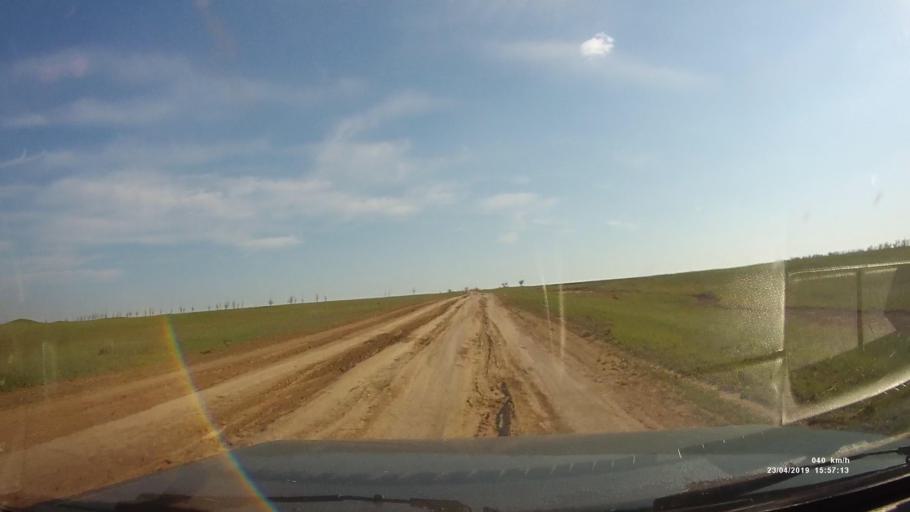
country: RU
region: Rostov
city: Remontnoye
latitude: 46.5330
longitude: 43.1103
